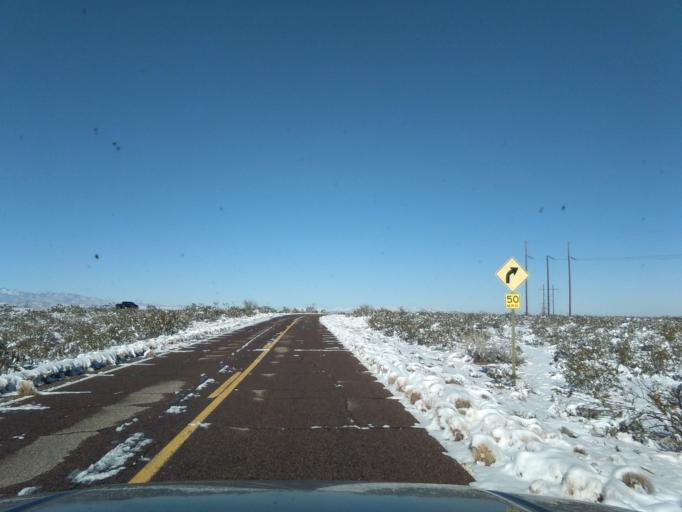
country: US
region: New Mexico
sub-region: Sierra County
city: Elephant Butte
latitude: 33.6127
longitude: -107.1471
